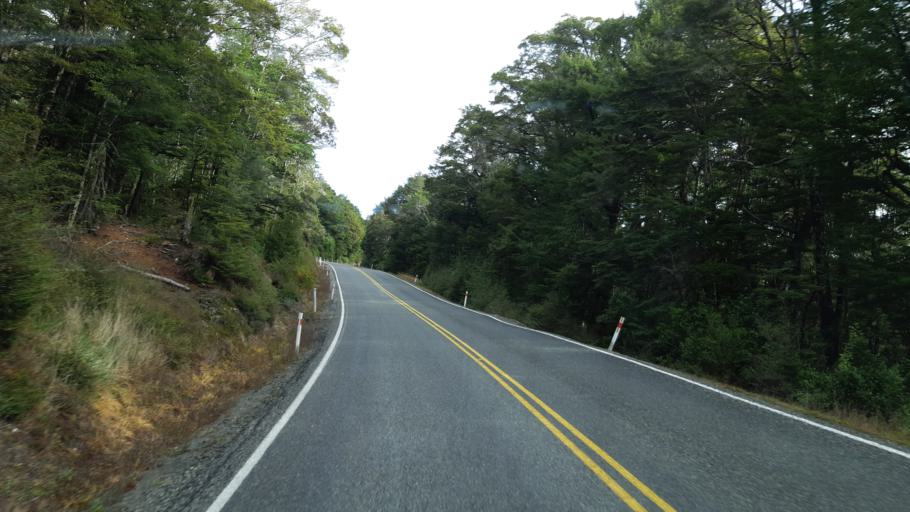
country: NZ
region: Tasman
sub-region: Tasman District
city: Wakefield
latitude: -41.7808
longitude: 172.9064
